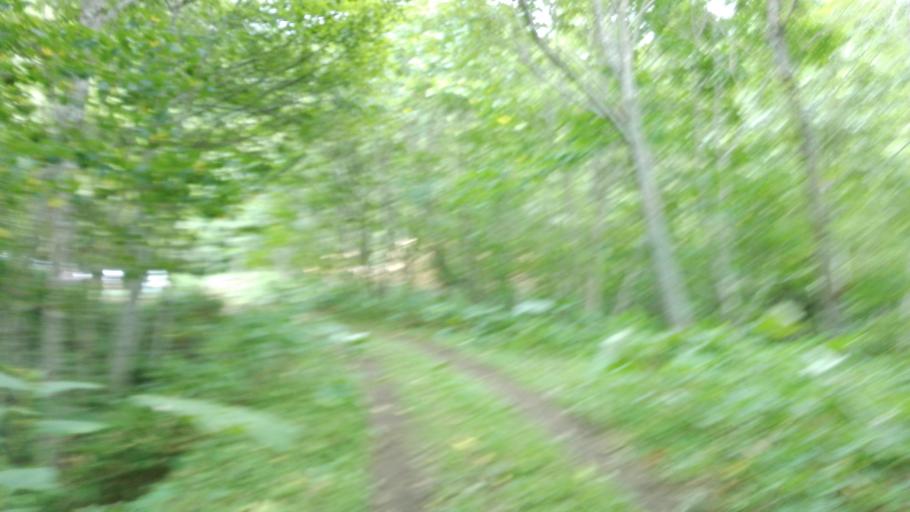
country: JP
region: Hokkaido
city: Sapporo
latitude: 42.9098
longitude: 141.1657
